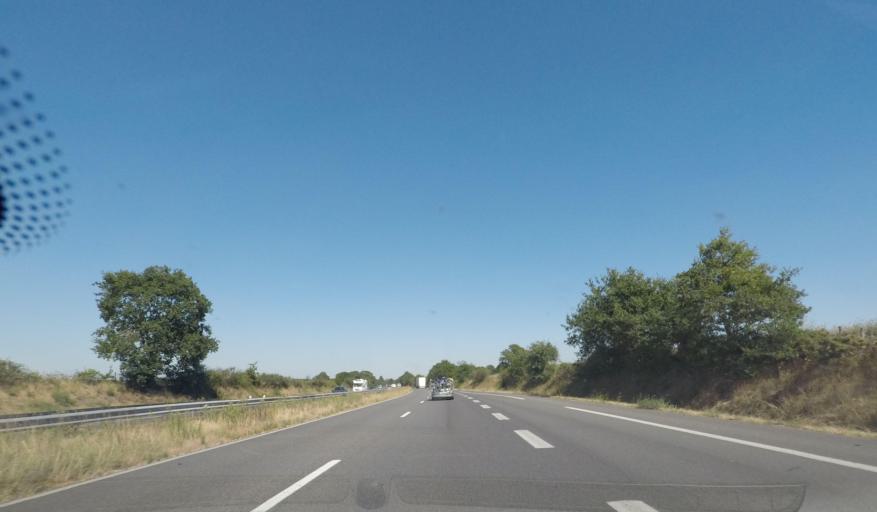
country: FR
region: Pays de la Loire
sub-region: Departement de la Loire-Atlantique
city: Pontchateau
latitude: 47.4468
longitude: -2.1168
